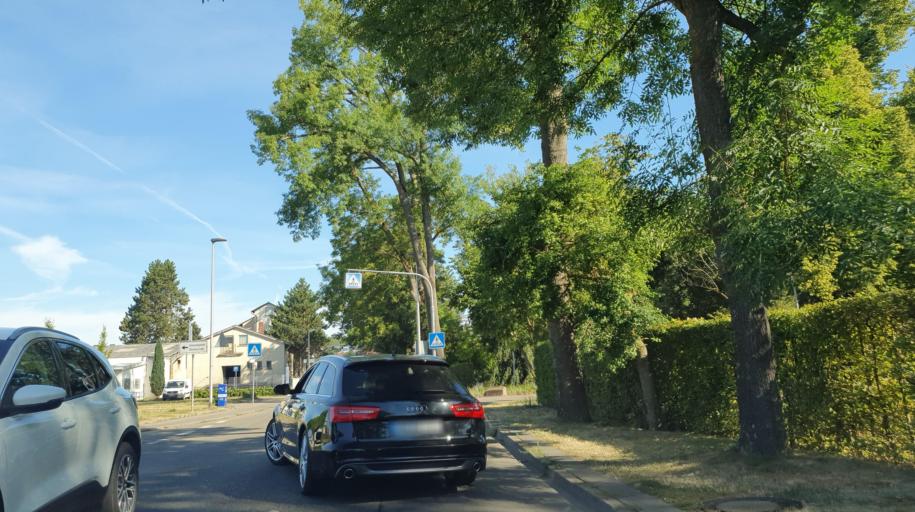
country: DE
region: Baden-Wuerttemberg
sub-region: Regierungsbezirk Stuttgart
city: Bad Rappenau
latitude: 49.2382
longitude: 9.0961
